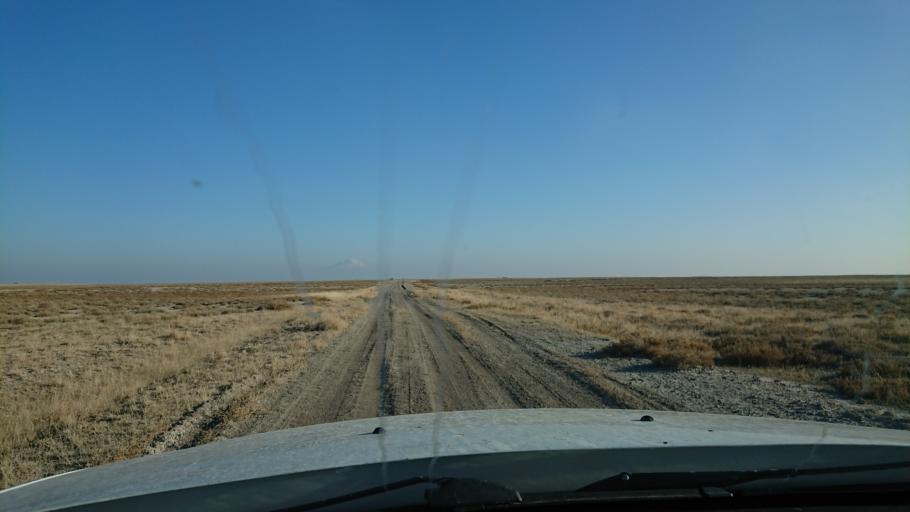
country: TR
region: Aksaray
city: Sultanhani
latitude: 38.4028
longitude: 33.5774
